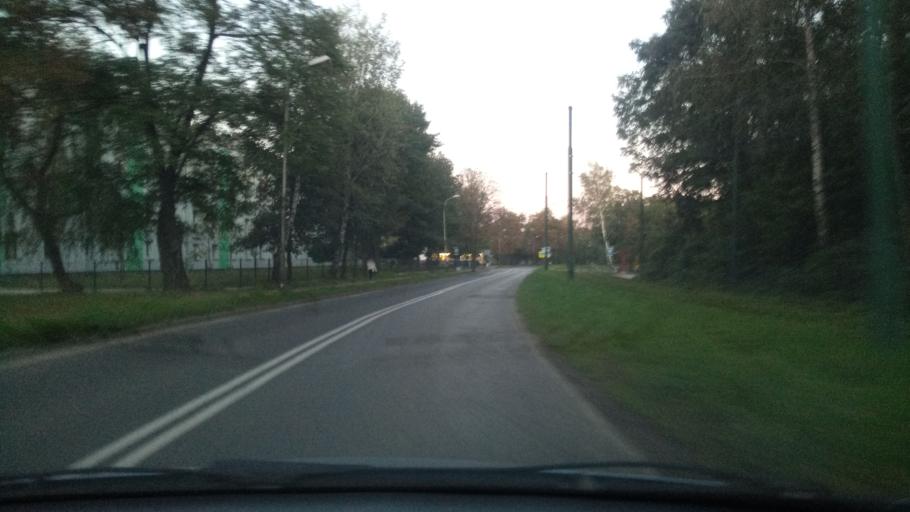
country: PL
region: Silesian Voivodeship
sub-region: Sosnowiec
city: Sosnowiec
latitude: 50.2901
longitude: 19.0926
